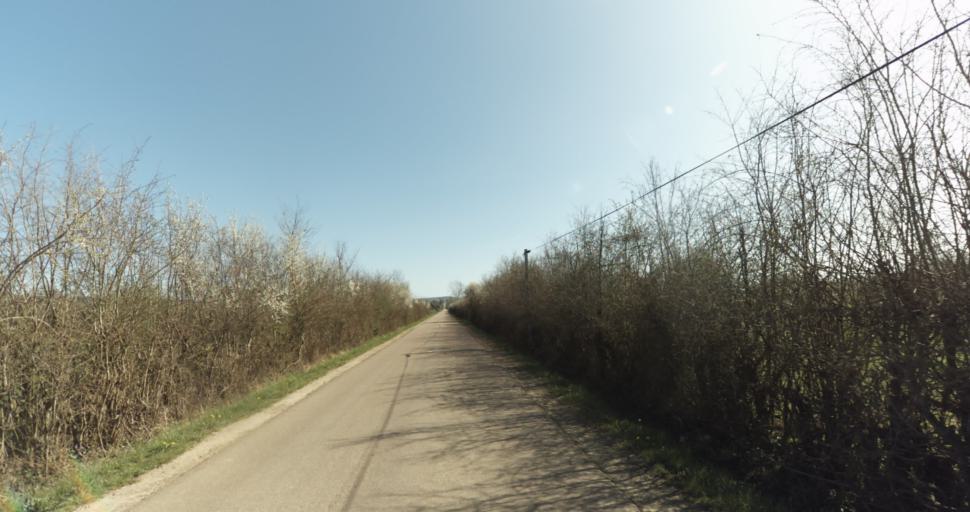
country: FR
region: Lower Normandy
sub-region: Departement du Calvados
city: Saint-Pierre-sur-Dives
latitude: 48.9517
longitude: 0.0118
